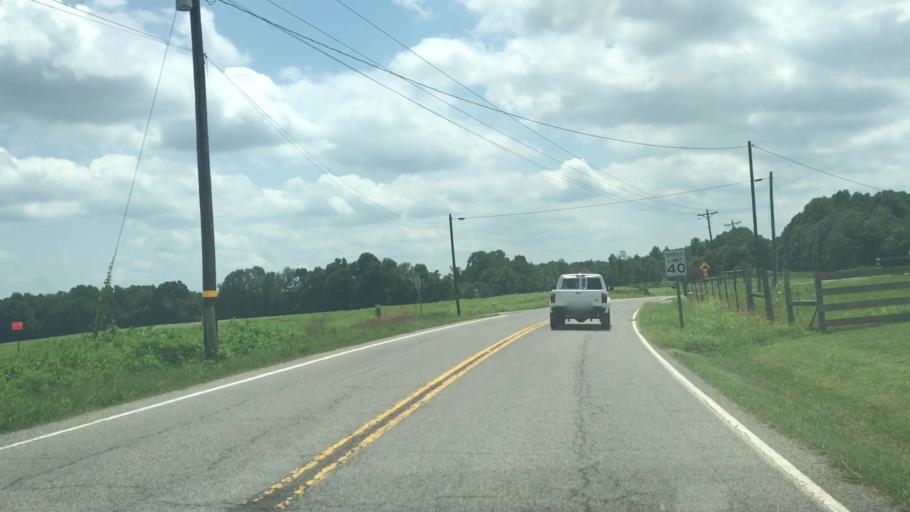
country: US
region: Tennessee
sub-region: Macon County
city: Red Boiling Springs
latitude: 36.4661
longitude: -85.8784
